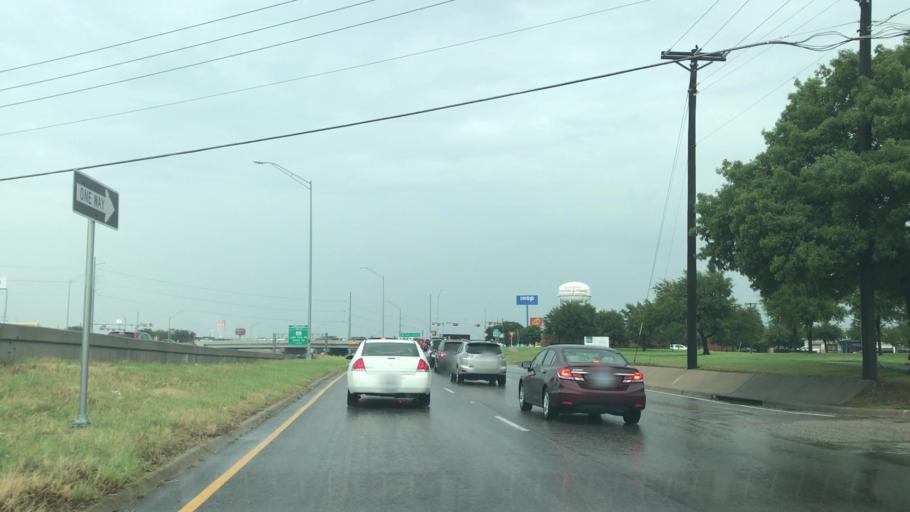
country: US
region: Texas
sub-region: Denton County
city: Lewisville
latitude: 33.0445
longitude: -97.0074
